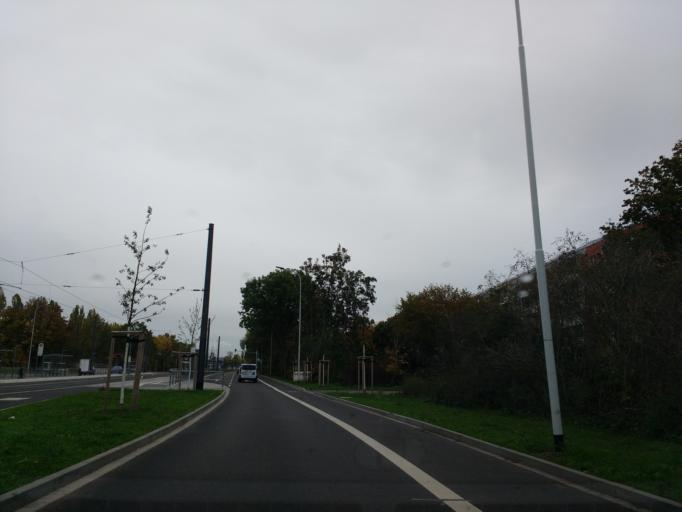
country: DE
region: Saxony-Anhalt
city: Halle Neustadt
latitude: 51.4873
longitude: 11.9455
